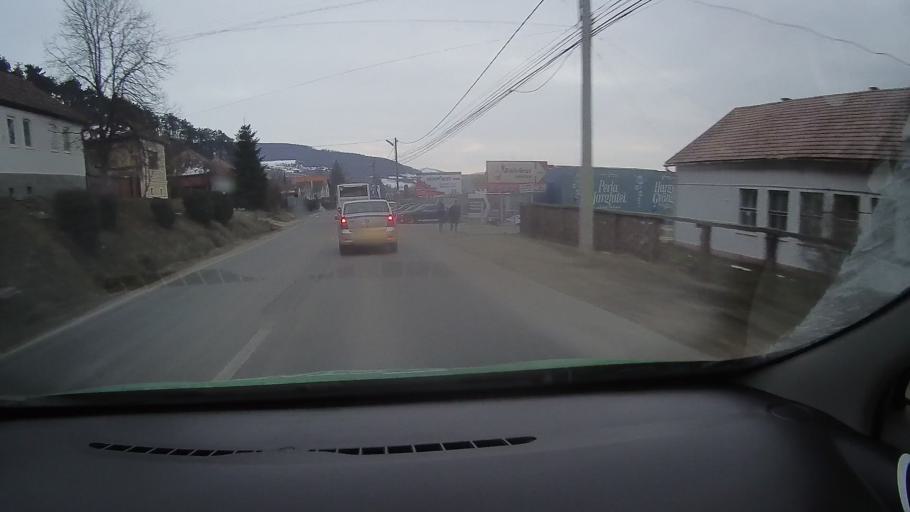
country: RO
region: Harghita
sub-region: Municipiul Odorheiu Secuiesc
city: Odorheiu Secuiesc
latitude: 46.2920
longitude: 25.2898
